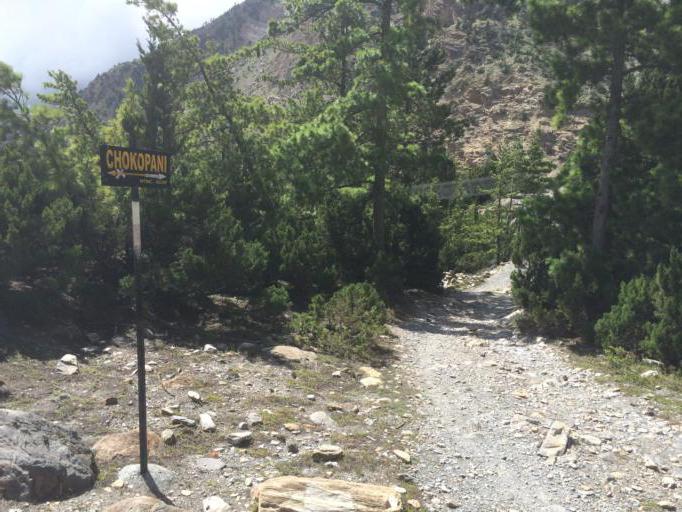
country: NP
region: Western Region
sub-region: Dhawalagiri Zone
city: Jomsom
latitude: 28.7214
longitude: 83.6715
